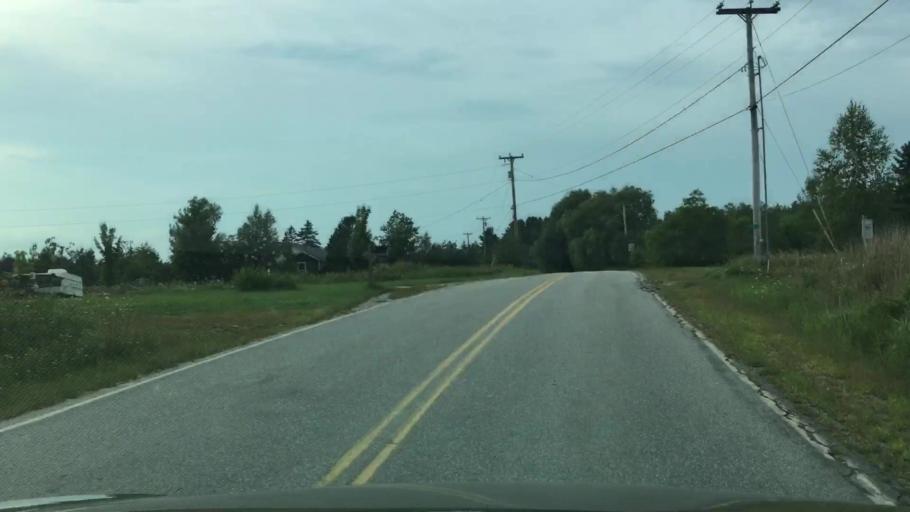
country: US
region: Maine
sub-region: Hancock County
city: Penobscot
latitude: 44.4687
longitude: -68.7400
